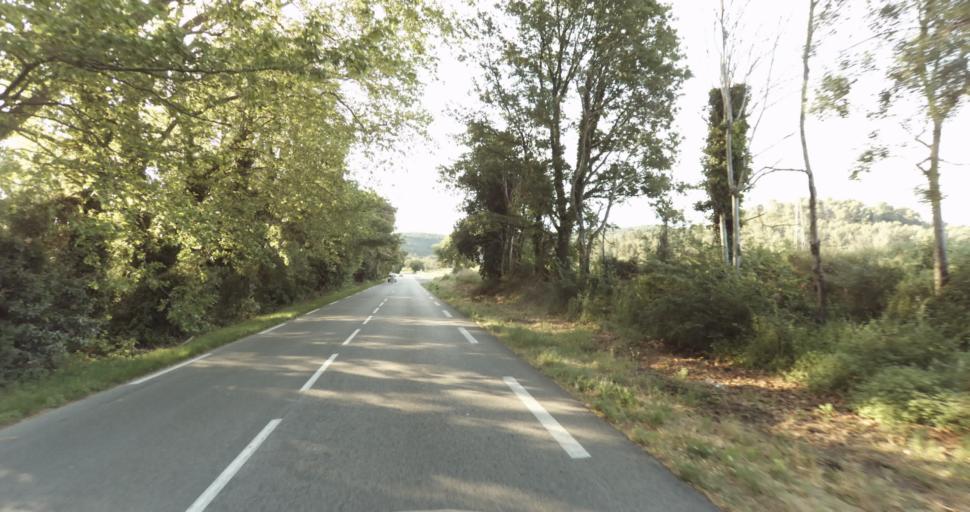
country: FR
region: Provence-Alpes-Cote d'Azur
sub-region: Departement du Var
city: Hyeres
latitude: 43.1477
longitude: 6.1496
